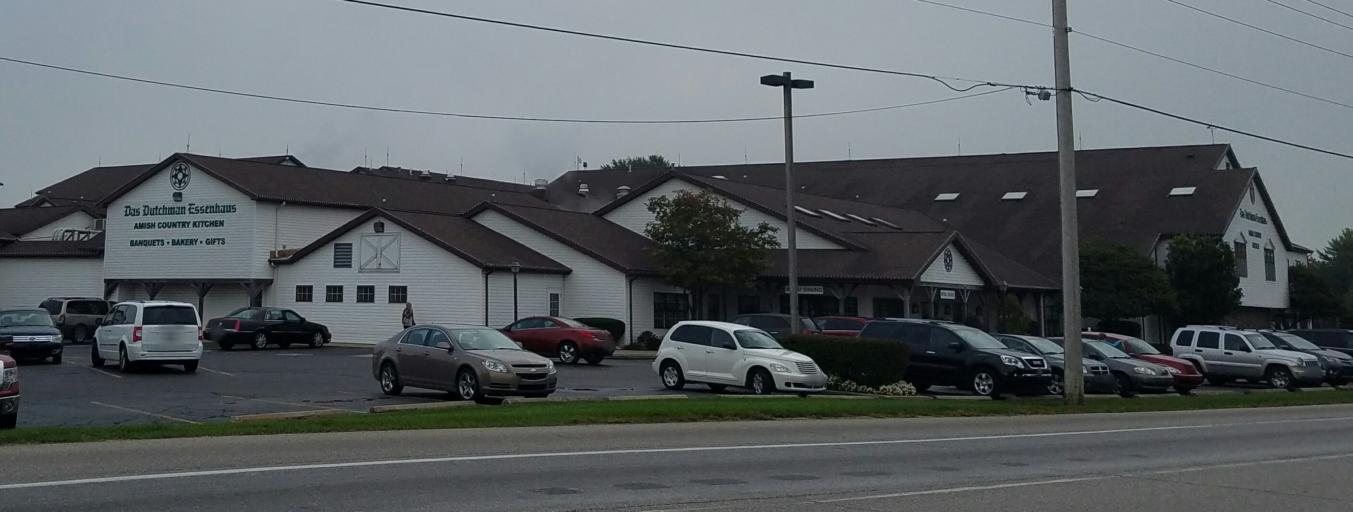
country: US
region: Indiana
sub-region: Elkhart County
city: Middlebury
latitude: 41.6679
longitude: -85.7271
